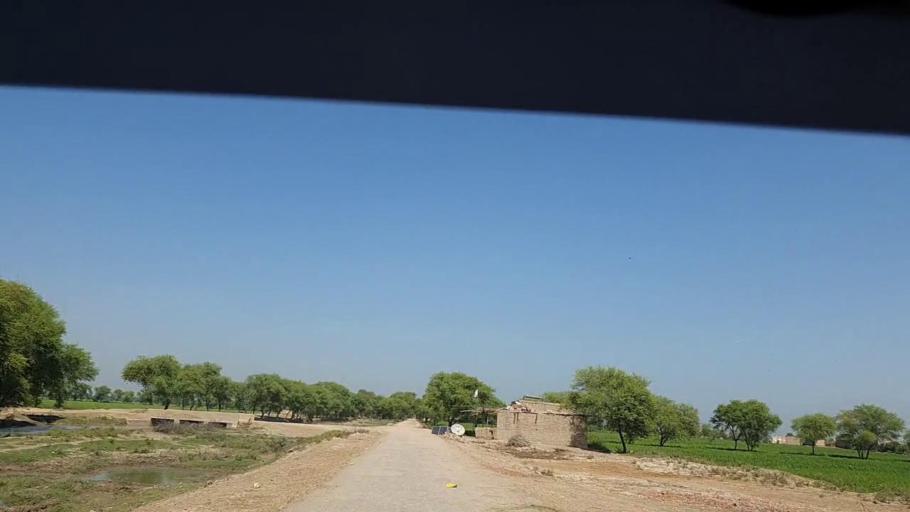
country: PK
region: Sindh
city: Tangwani
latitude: 28.2943
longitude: 69.0931
